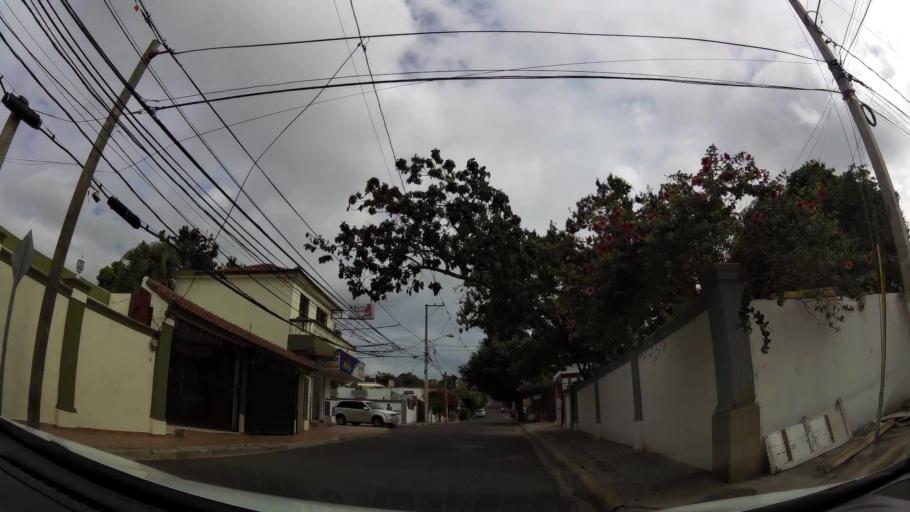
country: DO
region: Santiago
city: Santiago de los Caballeros
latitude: 19.4648
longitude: -70.6737
